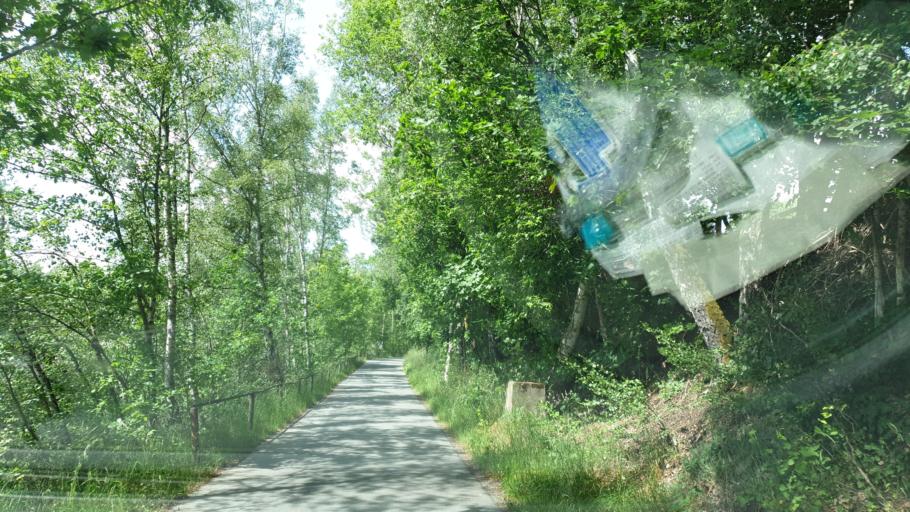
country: DE
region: Saxony
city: Adorf
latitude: 50.3323
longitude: 12.2583
